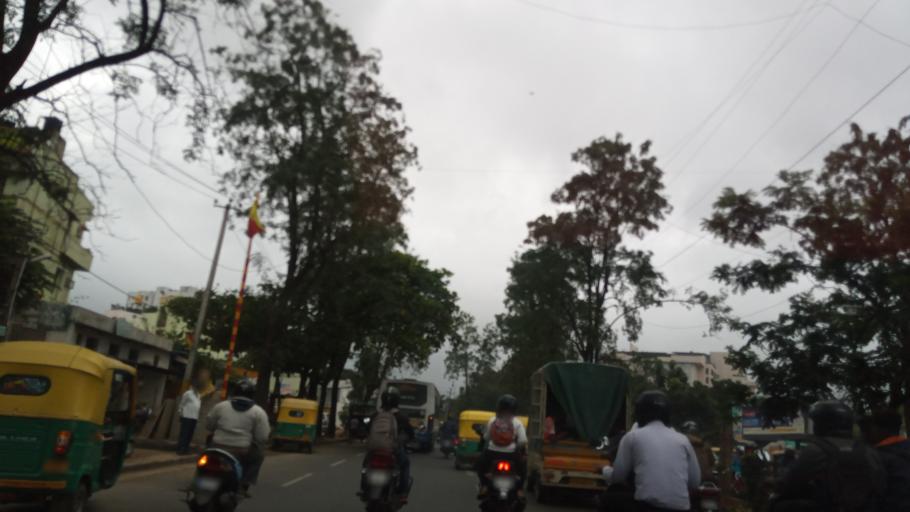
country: IN
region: Karnataka
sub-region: Bangalore Urban
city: Bangalore
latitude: 12.9381
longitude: 77.5336
